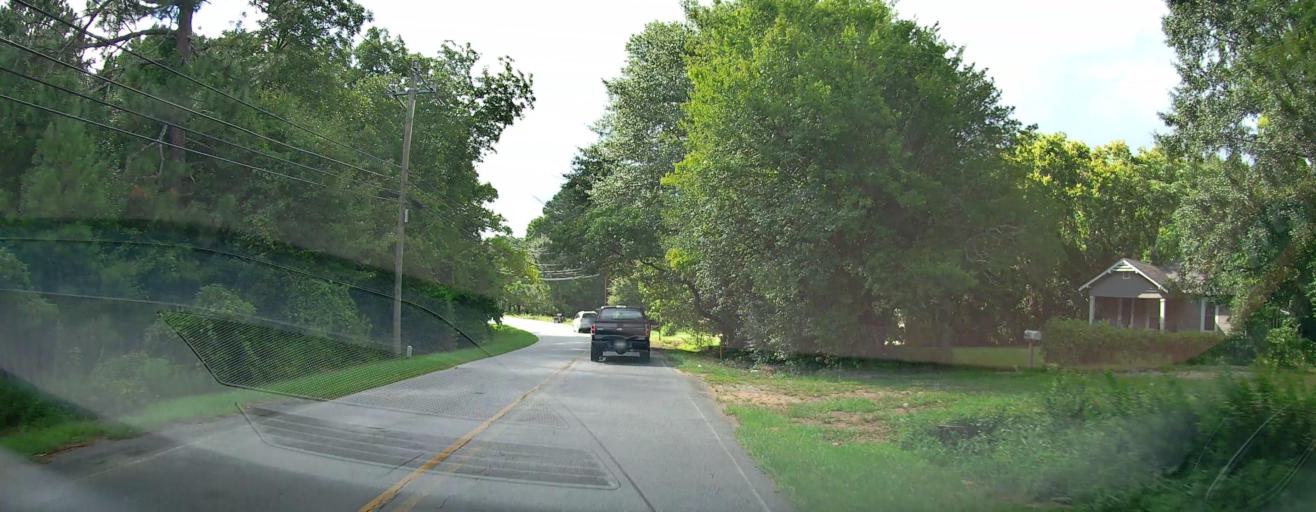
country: US
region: Alabama
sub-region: Russell County
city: Phenix City
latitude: 32.5218
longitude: -84.9712
